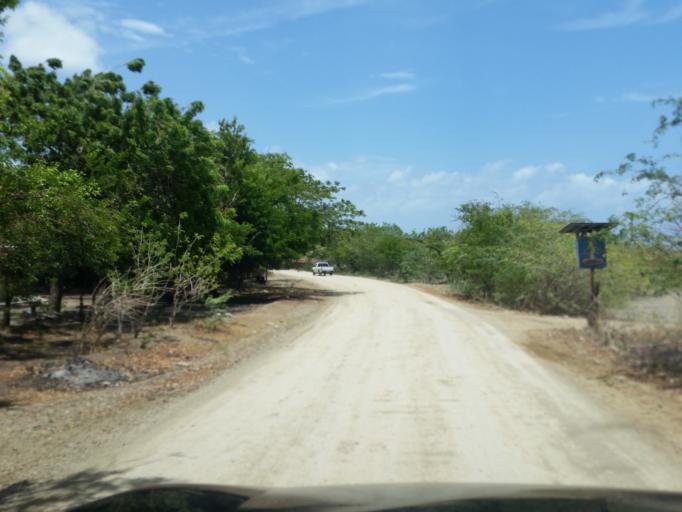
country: NI
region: Rivas
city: Tola
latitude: 11.4723
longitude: -86.1043
